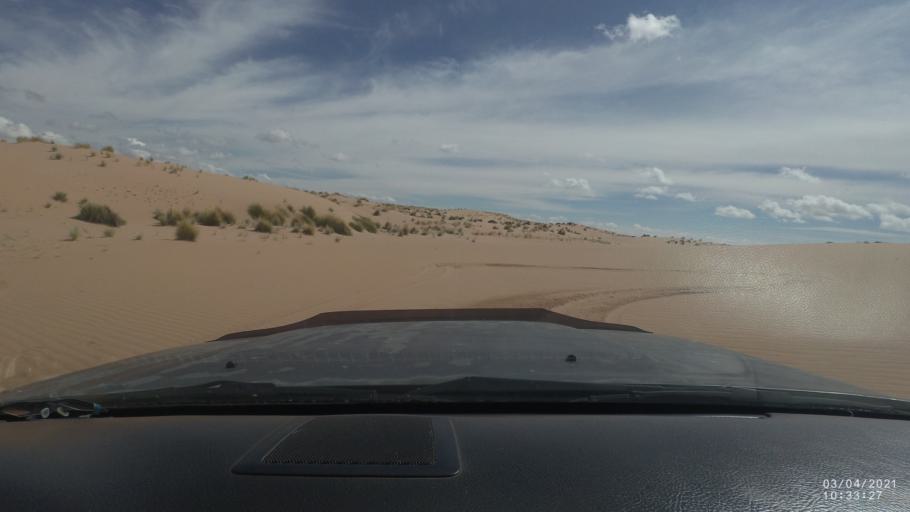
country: BO
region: Oruro
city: Poopo
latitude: -18.7053
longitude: -67.5204
